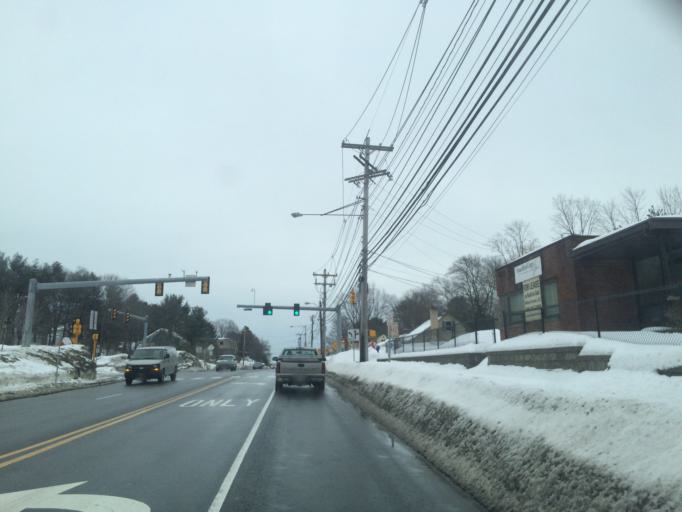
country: US
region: Massachusetts
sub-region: Middlesex County
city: Waltham
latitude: 42.3765
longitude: -71.2635
